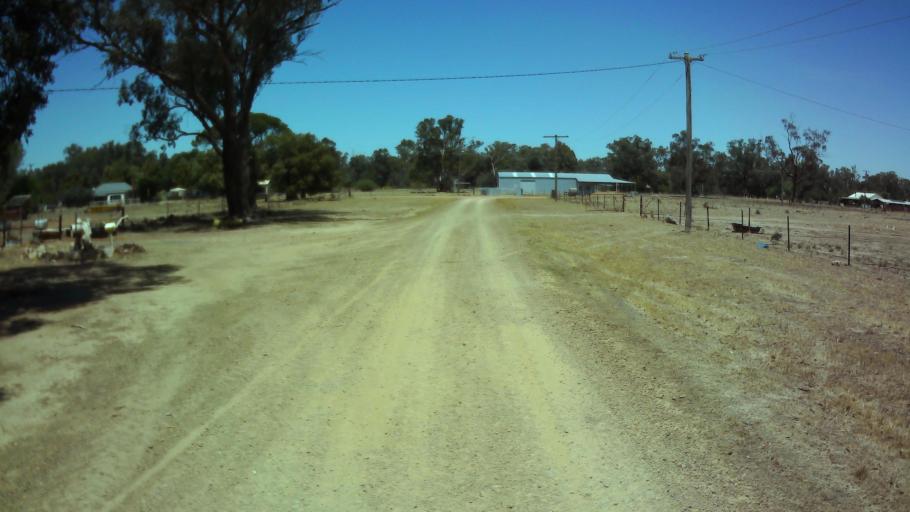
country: AU
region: New South Wales
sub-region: Weddin
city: Grenfell
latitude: -34.0365
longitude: 147.9291
